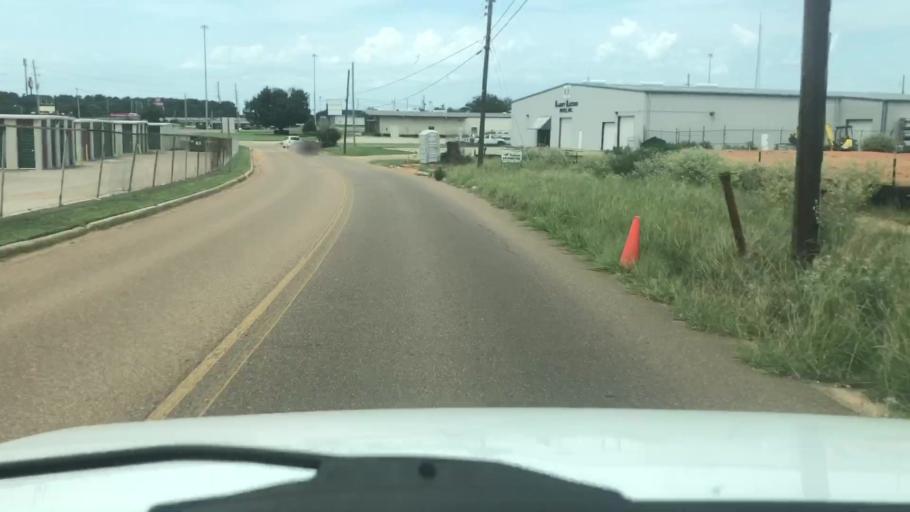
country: US
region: Texas
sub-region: Bowie County
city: Wake Village
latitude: 33.4432
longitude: -94.0917
